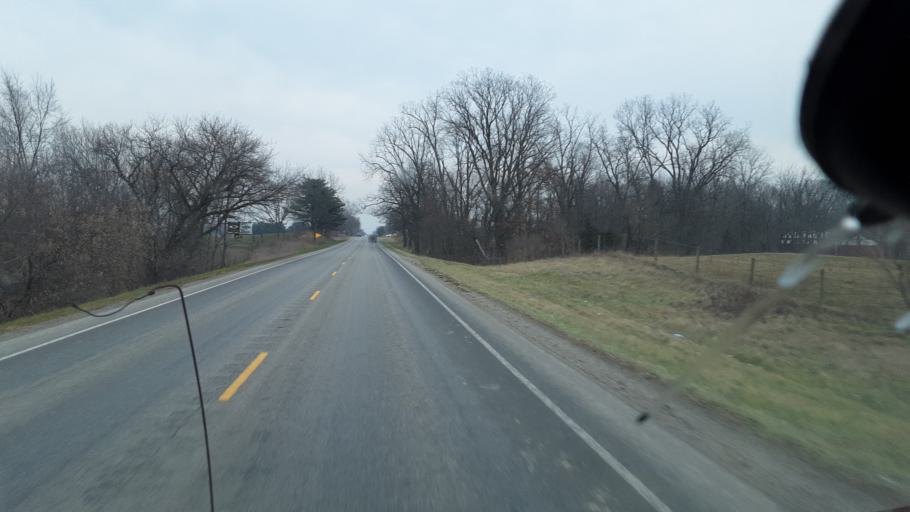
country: US
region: Michigan
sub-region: Saint Joseph County
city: White Pigeon
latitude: 41.7263
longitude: -85.6247
